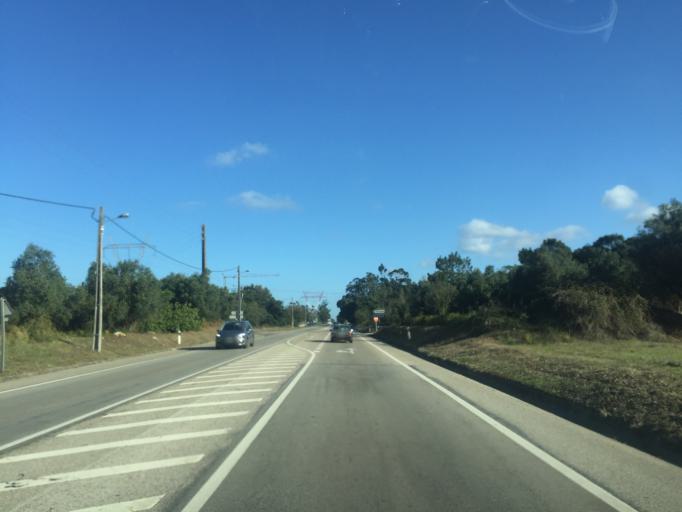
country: PT
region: Leiria
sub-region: Alcobaca
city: Turquel
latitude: 39.4645
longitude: -8.9437
